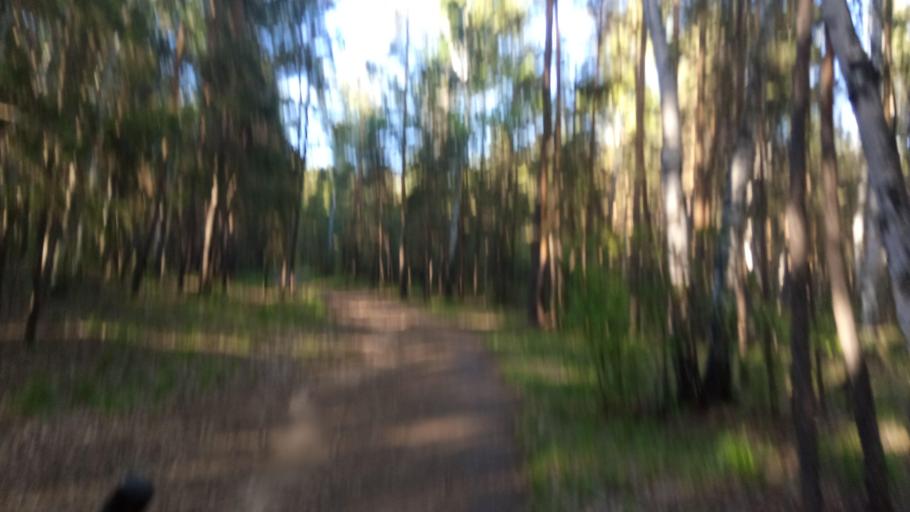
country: RU
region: Chelyabinsk
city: Novosineglazovskiy
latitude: 55.1224
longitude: 61.3404
